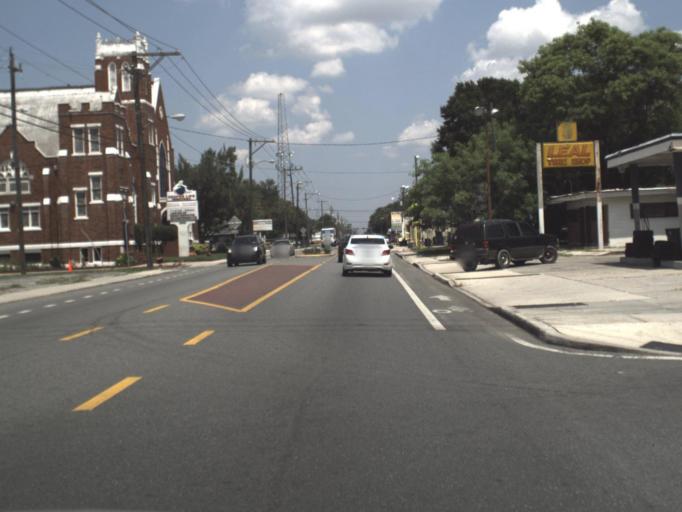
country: US
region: Florida
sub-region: Hillsborough County
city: Tampa
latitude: 27.9727
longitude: -82.4512
